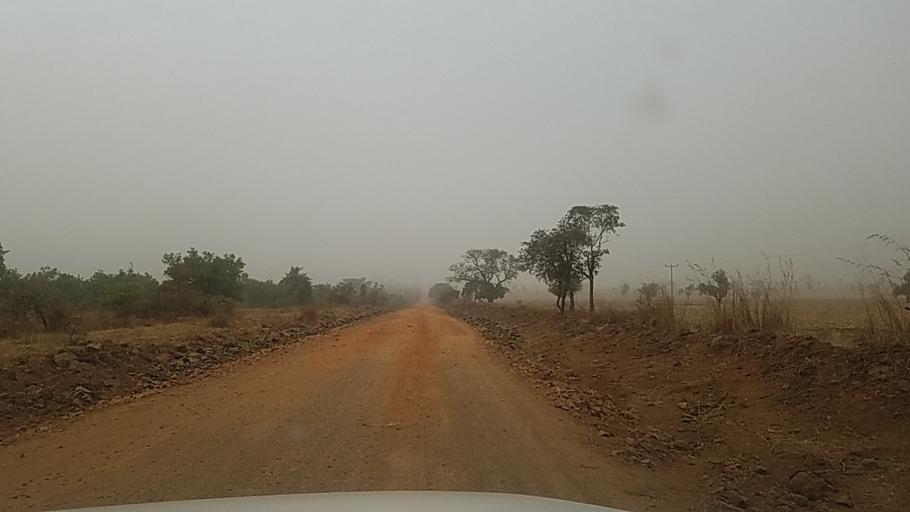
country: ET
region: Amhara
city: Bure
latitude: 10.9433
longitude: 36.4765
